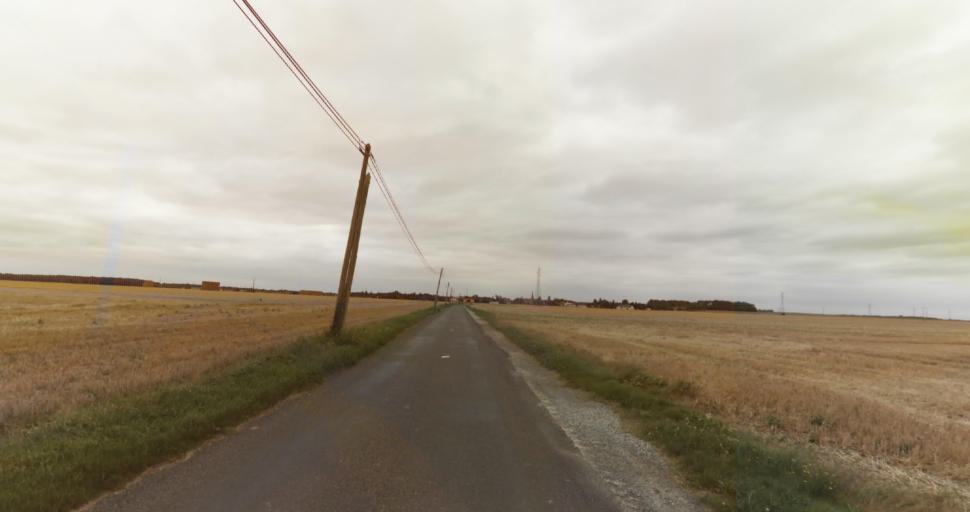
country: FR
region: Haute-Normandie
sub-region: Departement de l'Eure
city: Menilles
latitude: 48.9481
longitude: 1.2654
